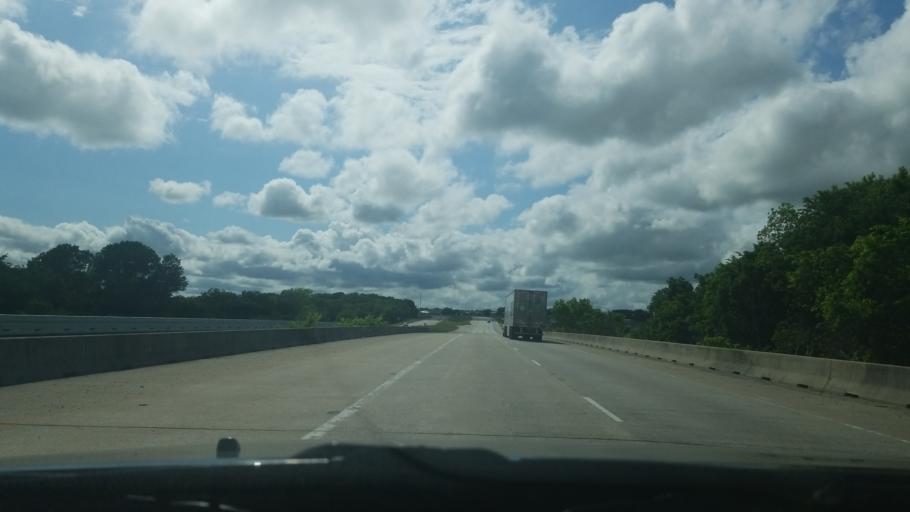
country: US
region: Texas
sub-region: Denton County
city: Ponder
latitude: 33.2493
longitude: -97.4034
